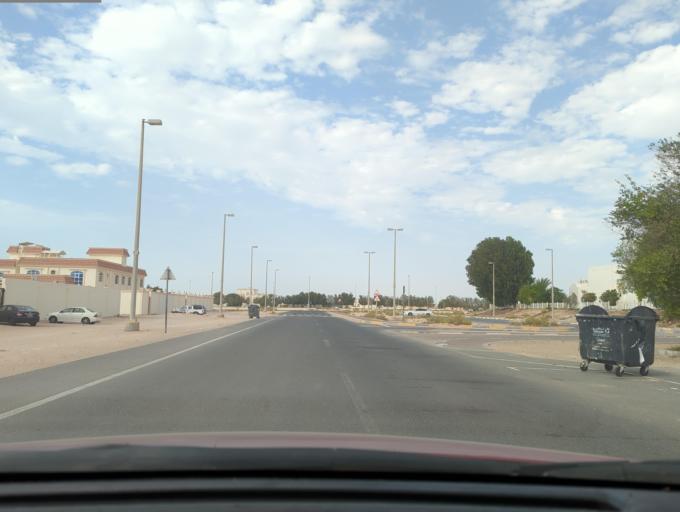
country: AE
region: Abu Dhabi
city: Abu Dhabi
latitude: 24.3829
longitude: 54.6999
